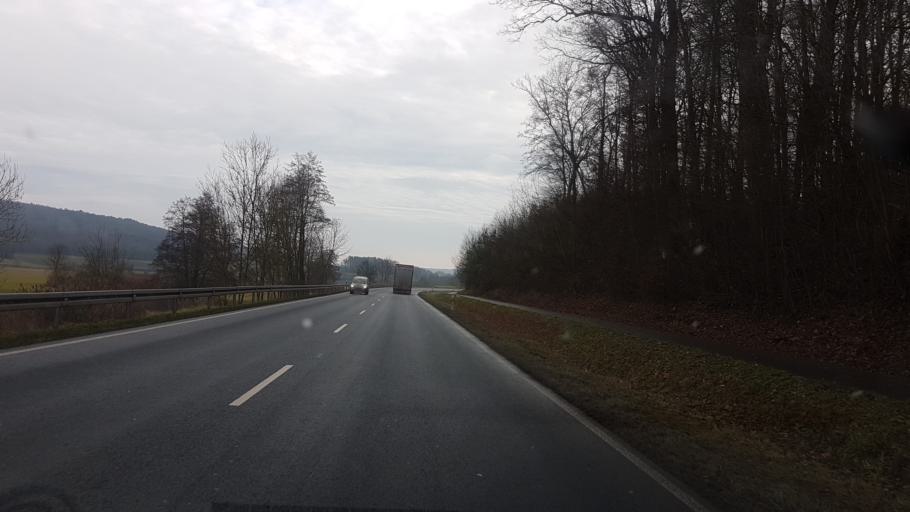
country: DE
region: Bavaria
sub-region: Regierungsbezirk Unterfranken
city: Rentweinsdorf
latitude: 50.0571
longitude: 10.8086
